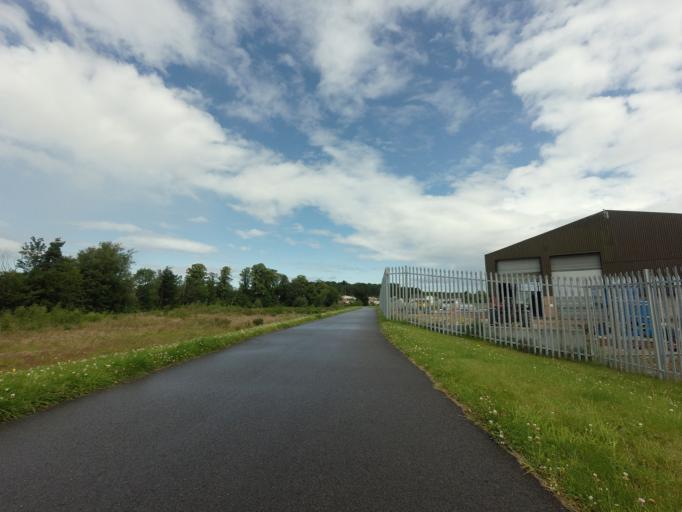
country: GB
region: Scotland
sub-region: Moray
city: Elgin
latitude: 57.6507
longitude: -3.2963
